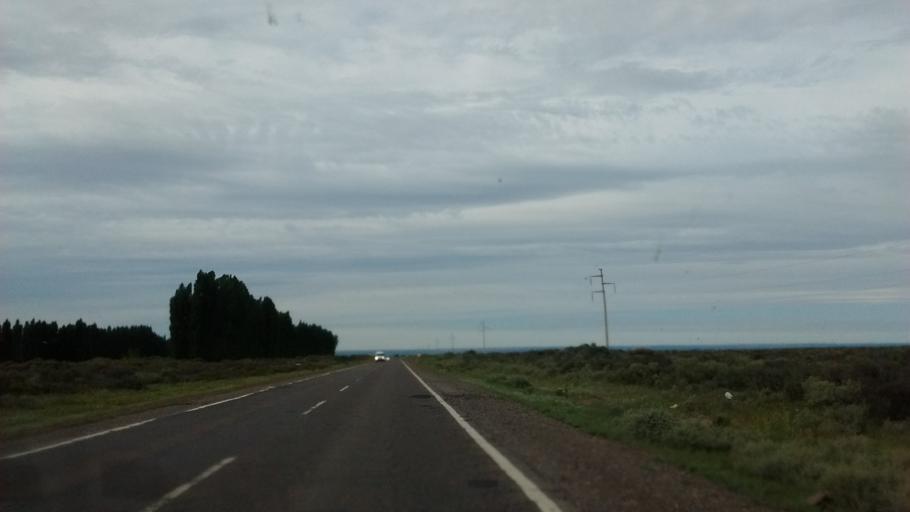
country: AR
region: Rio Negro
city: Catriel
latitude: -37.9355
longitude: -67.8819
